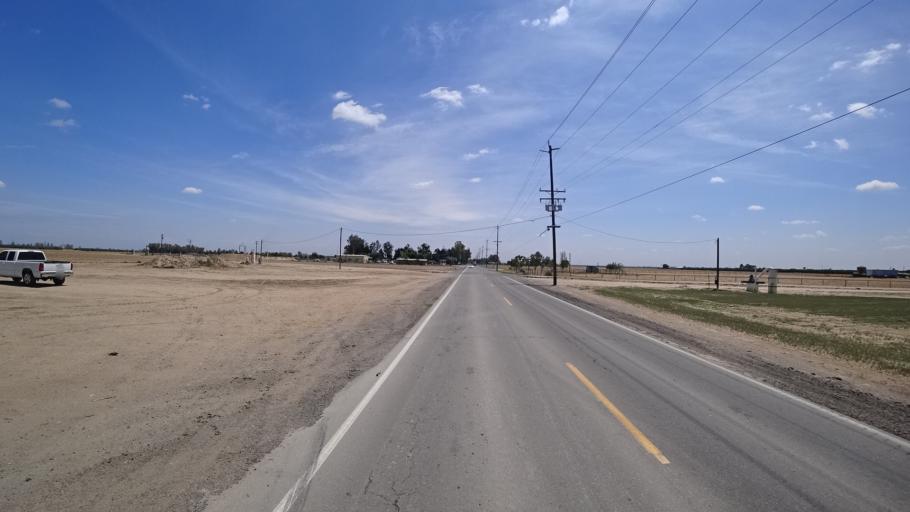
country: US
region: California
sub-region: Kings County
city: Home Garden
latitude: 36.2986
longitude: -119.6273
